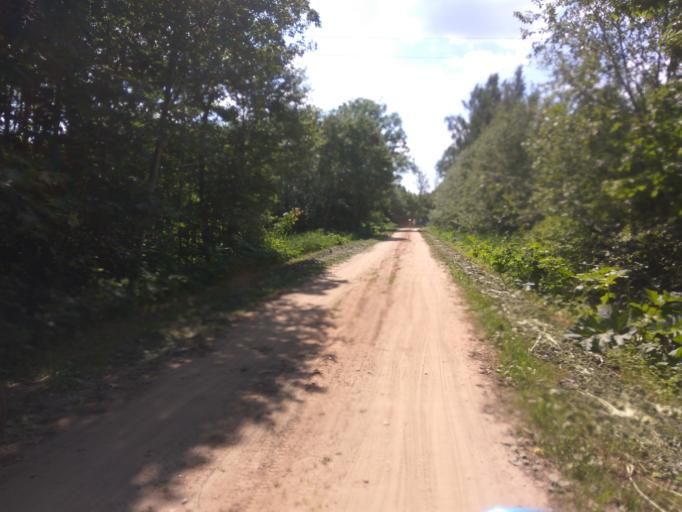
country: LV
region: Kuldigas Rajons
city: Kuldiga
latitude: 56.9247
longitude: 21.9734
